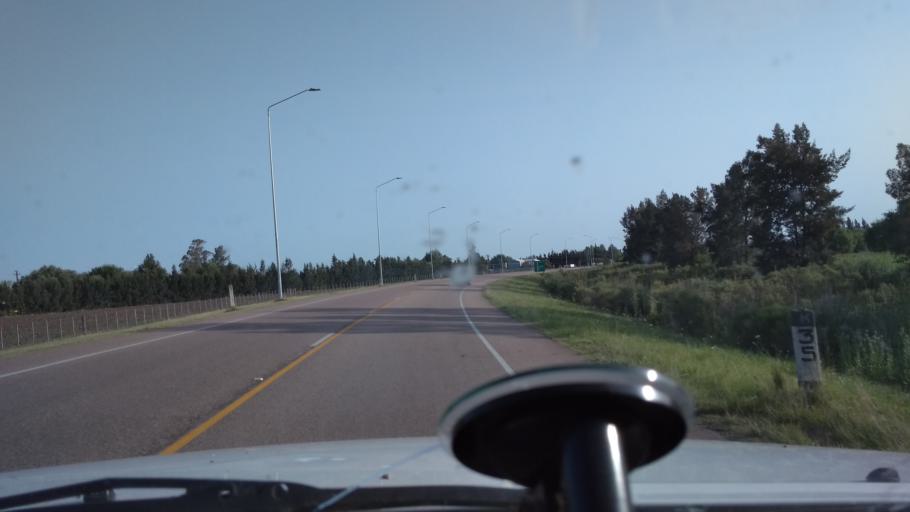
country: UY
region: Canelones
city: Sauce
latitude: -34.6457
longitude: -56.0496
